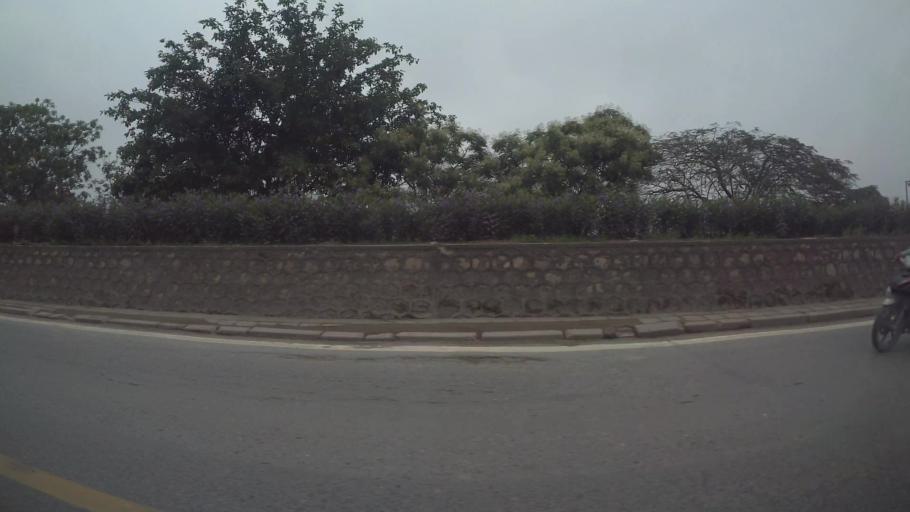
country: VN
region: Hung Yen
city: Van Giang
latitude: 20.9791
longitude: 105.8924
